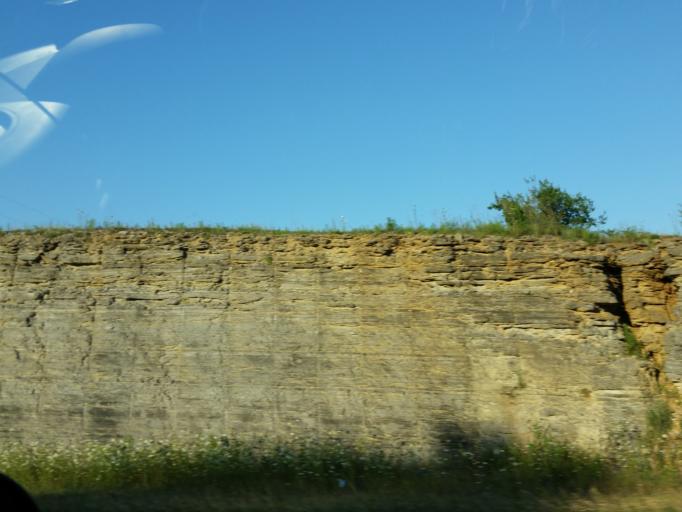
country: US
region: Tennessee
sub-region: Rutherford County
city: Smyrna
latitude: 36.0171
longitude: -86.4276
